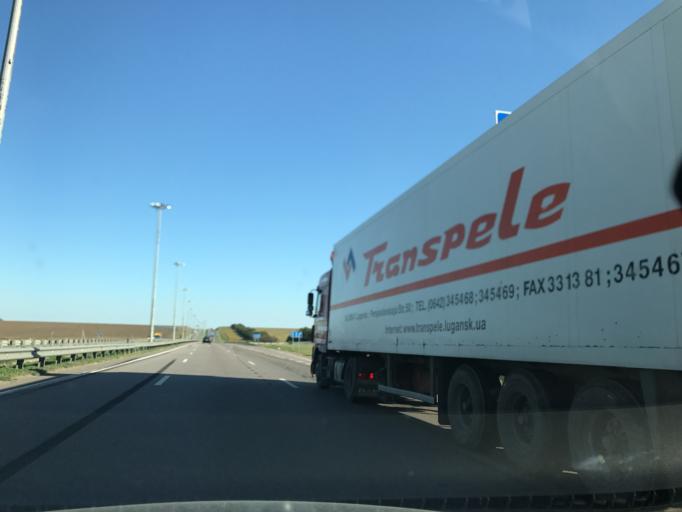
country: RU
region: Rostov
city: Glubokiy
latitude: 48.4506
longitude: 40.3408
